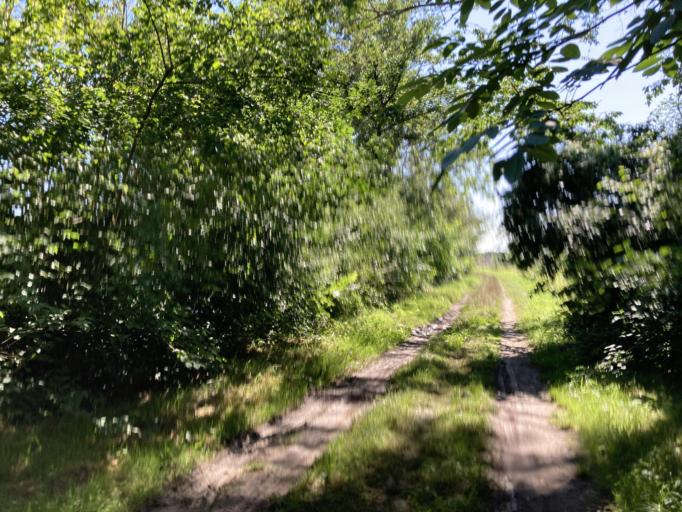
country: FR
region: Bourgogne
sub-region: Departement de l'Yonne
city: Laroche-Saint-Cydroine
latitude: 47.9626
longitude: 3.4617
